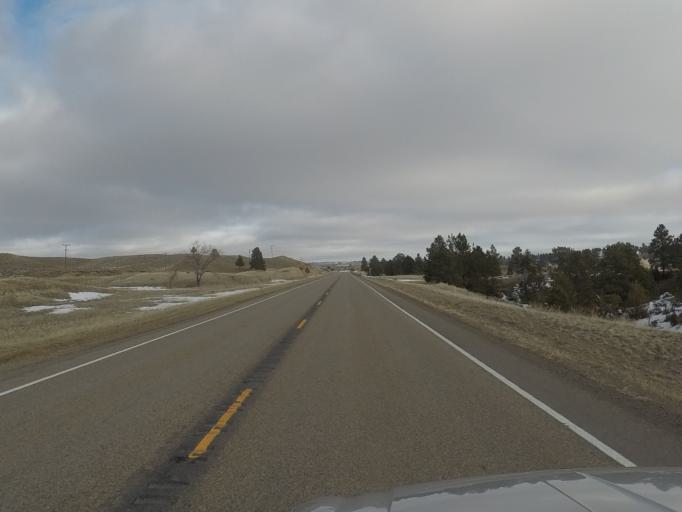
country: US
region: Montana
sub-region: Golden Valley County
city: Ryegate
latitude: 46.3028
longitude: -109.3369
